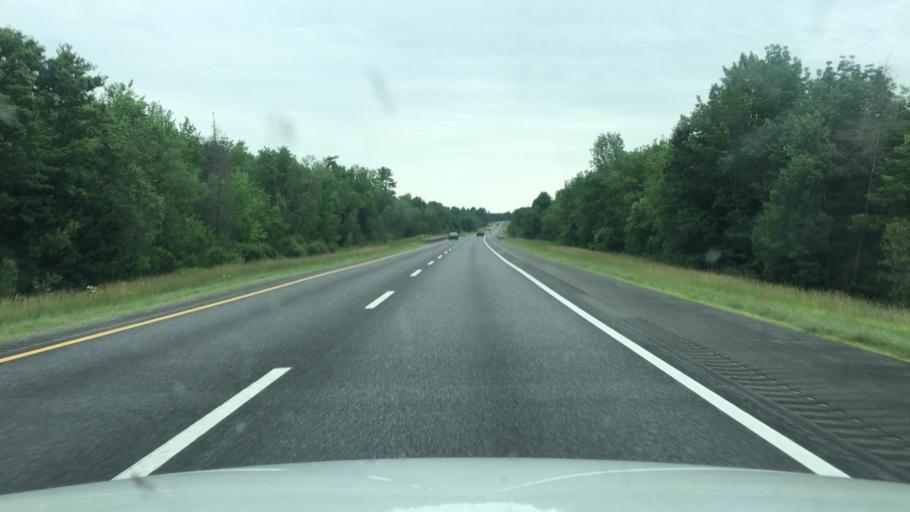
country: US
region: Maine
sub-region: Sagadahoc County
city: Richmond
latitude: 44.0792
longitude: -69.8784
